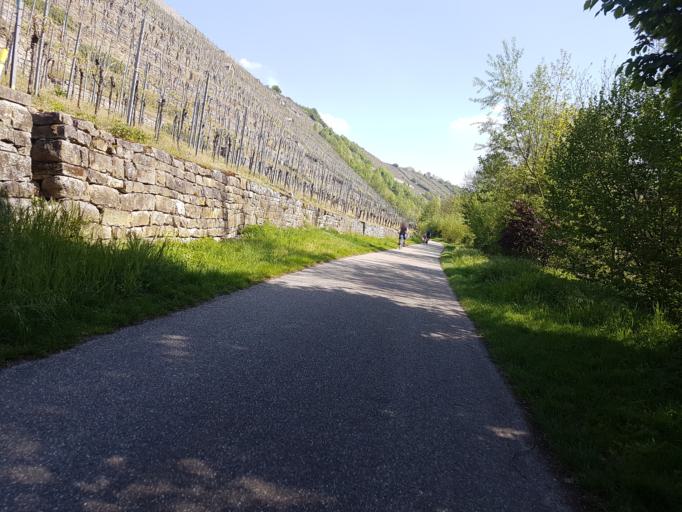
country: DE
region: Baden-Wuerttemberg
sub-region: Regierungsbezirk Stuttgart
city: Besigheim
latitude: 48.9926
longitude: 9.1482
